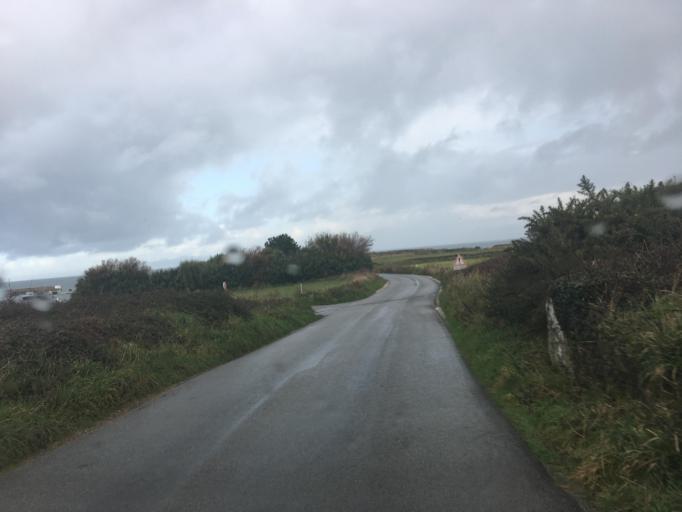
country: FR
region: Lower Normandy
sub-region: Departement de la Manche
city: Reville
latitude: 49.6918
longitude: -1.2777
